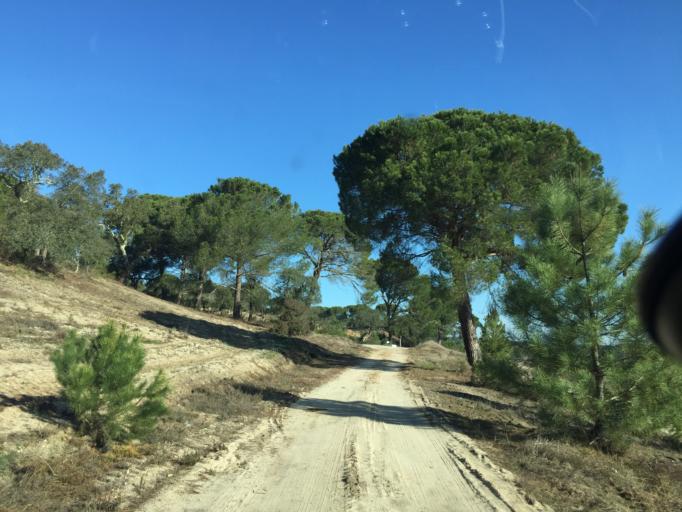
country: PT
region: Portalegre
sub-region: Ponte de Sor
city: Santo Andre
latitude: 39.0120
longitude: -8.2848
